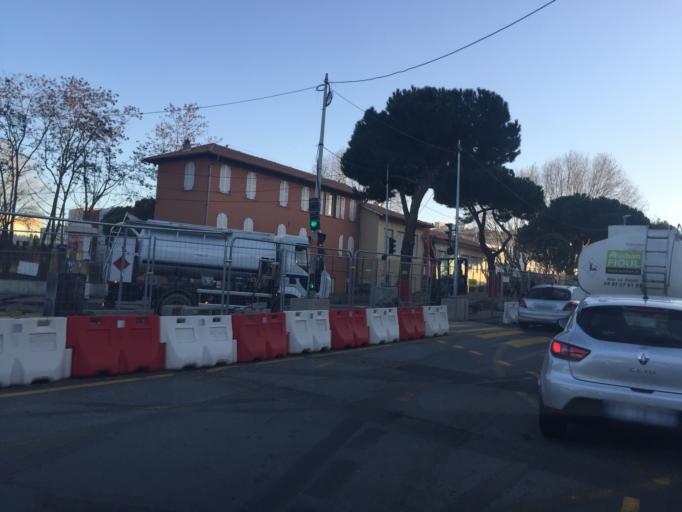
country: FR
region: Provence-Alpes-Cote d'Azur
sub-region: Departement des Alpes-Maritimes
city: Saint-Laurent-du-Var
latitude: 43.6768
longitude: 7.2015
